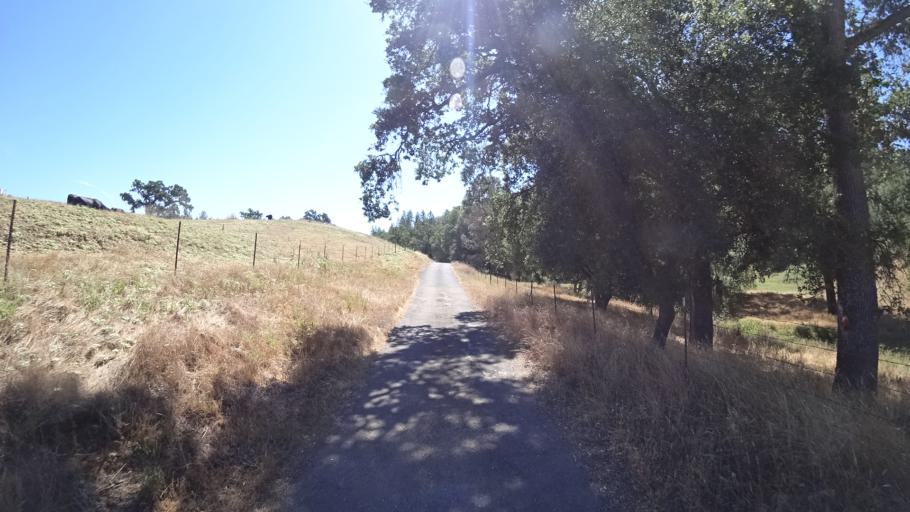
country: US
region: California
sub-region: Calaveras County
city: Angels Camp
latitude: 38.1408
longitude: -120.5474
